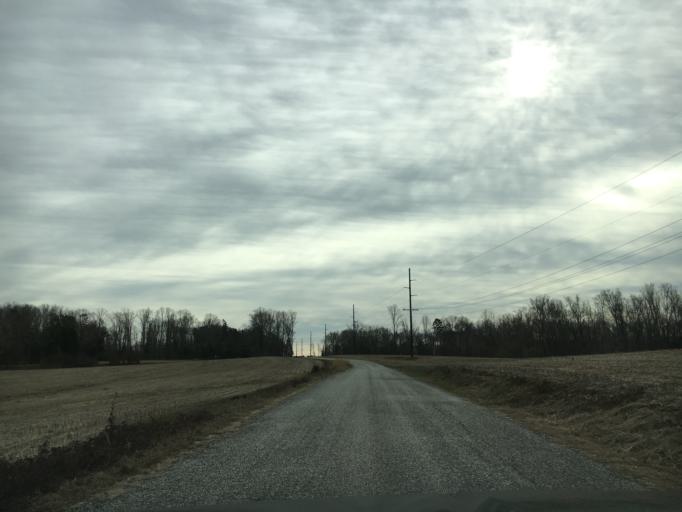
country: US
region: Virginia
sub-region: Powhatan County
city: Powhatan
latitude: 37.4801
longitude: -77.9676
